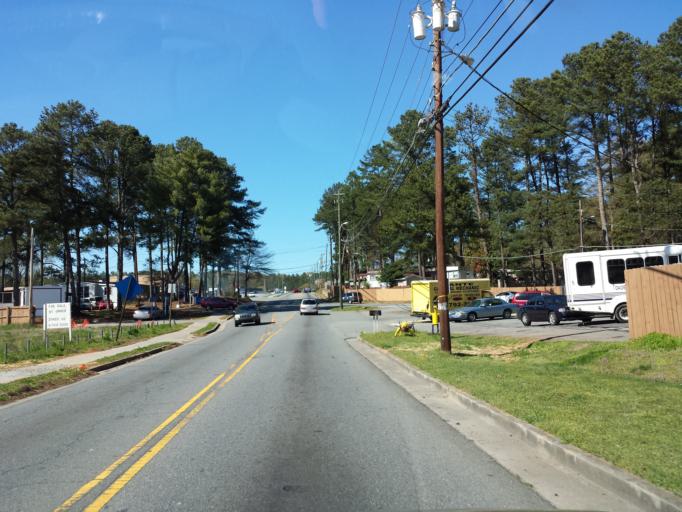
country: US
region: Georgia
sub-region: Cobb County
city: Fair Oaks
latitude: 33.9318
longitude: -84.5553
